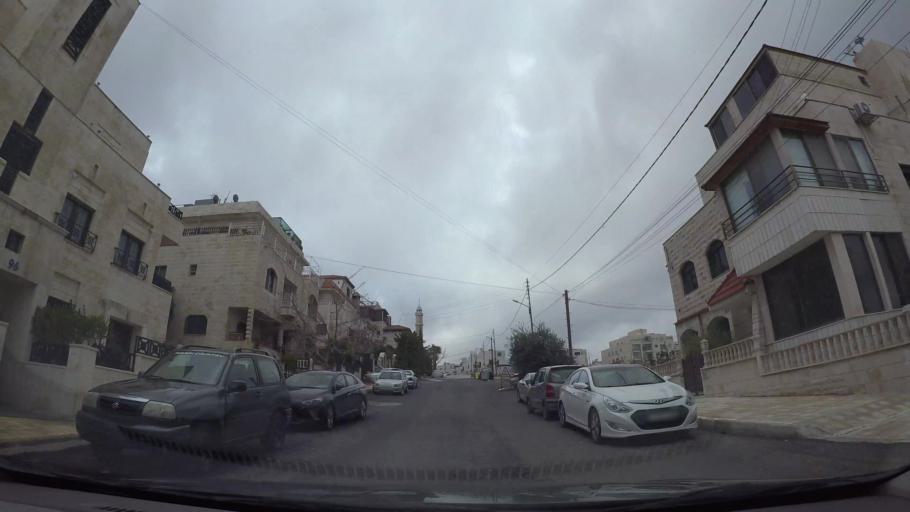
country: JO
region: Amman
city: Amman
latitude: 31.9413
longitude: 35.9051
